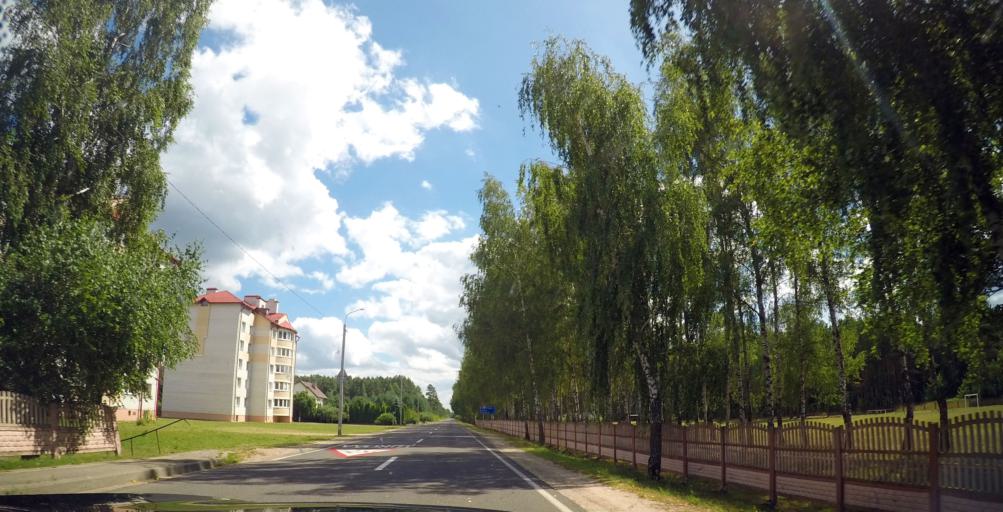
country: LT
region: Alytaus apskritis
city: Druskininkai
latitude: 53.8797
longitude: 24.1411
